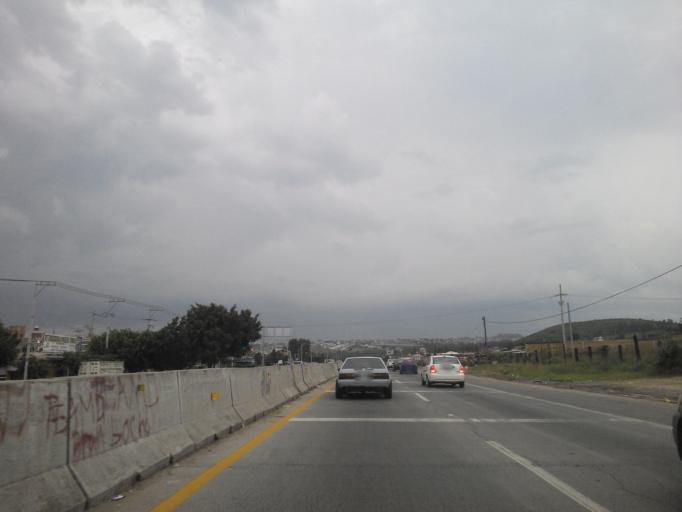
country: MX
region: Jalisco
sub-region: Tonala
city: Colonia Guadalupana
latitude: 20.5928
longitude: -103.2259
